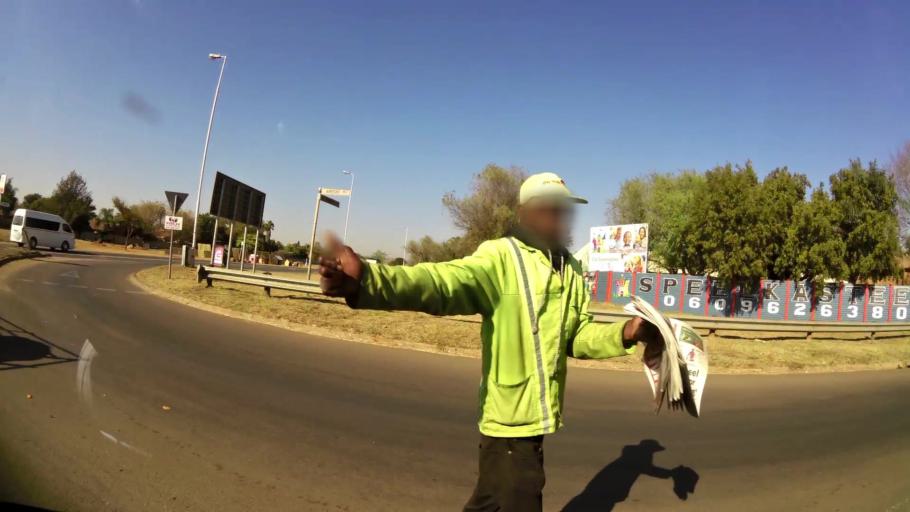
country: ZA
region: Gauteng
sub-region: City of Tshwane Metropolitan Municipality
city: Pretoria
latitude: -25.6496
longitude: 28.2445
